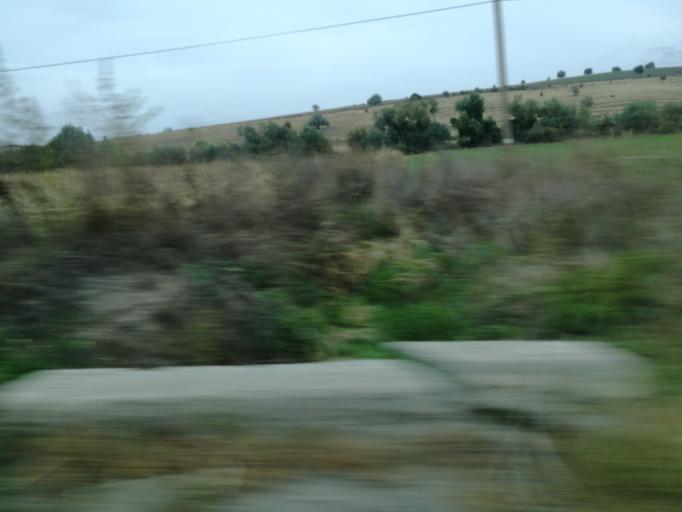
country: RO
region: Tulcea
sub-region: Comuna Ciucurova
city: Ciucurova
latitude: 44.9233
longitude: 28.4516
